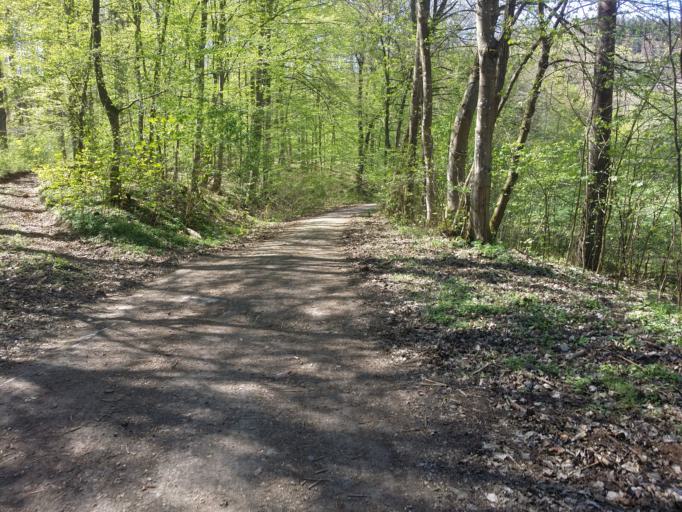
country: DE
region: Saxony-Anhalt
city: Ballenstedt
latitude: 51.6747
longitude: 11.2181
